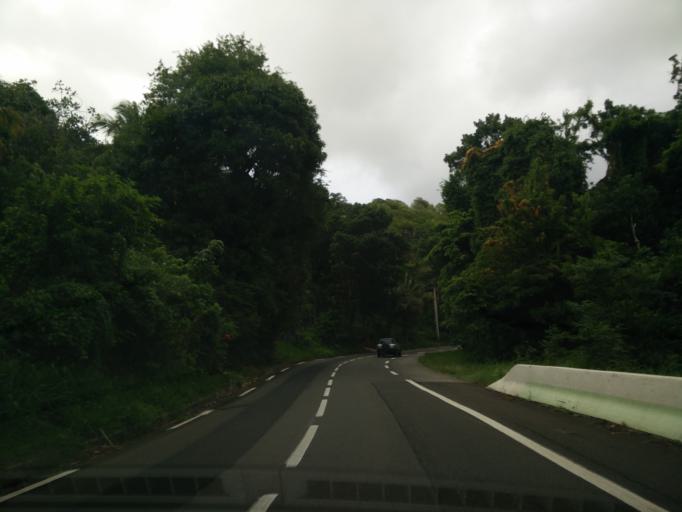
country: MQ
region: Martinique
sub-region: Martinique
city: Le Marin
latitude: 14.4771
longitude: -60.8625
